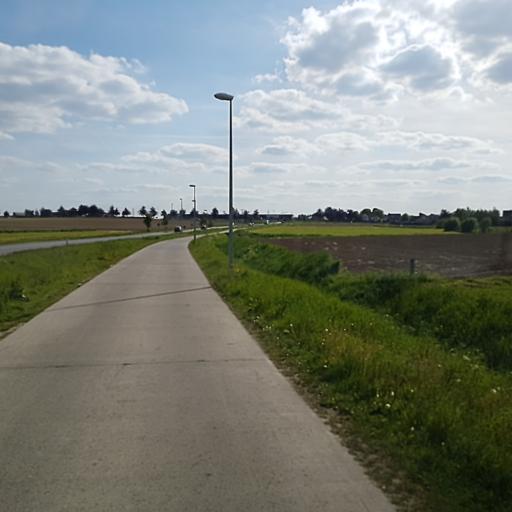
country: BE
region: Flanders
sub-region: Provincie West-Vlaanderen
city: Tielt
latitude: 50.9885
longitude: 3.3443
